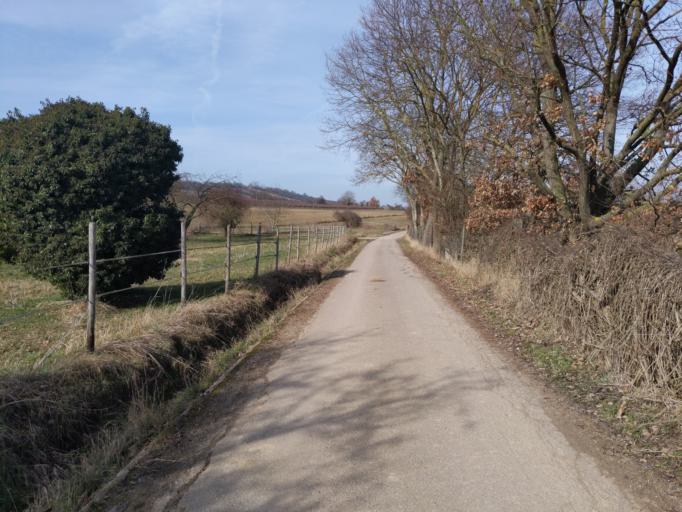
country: DE
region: Rheinland-Pfalz
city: Ingelheim am Rhein
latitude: 49.9458
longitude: 8.0656
